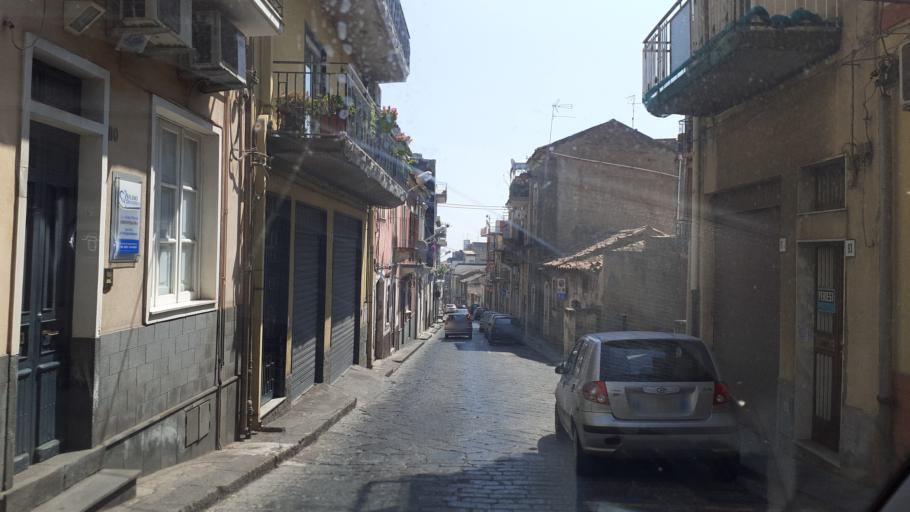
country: IT
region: Sicily
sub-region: Catania
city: Misterbianco
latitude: 37.5189
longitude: 15.0111
